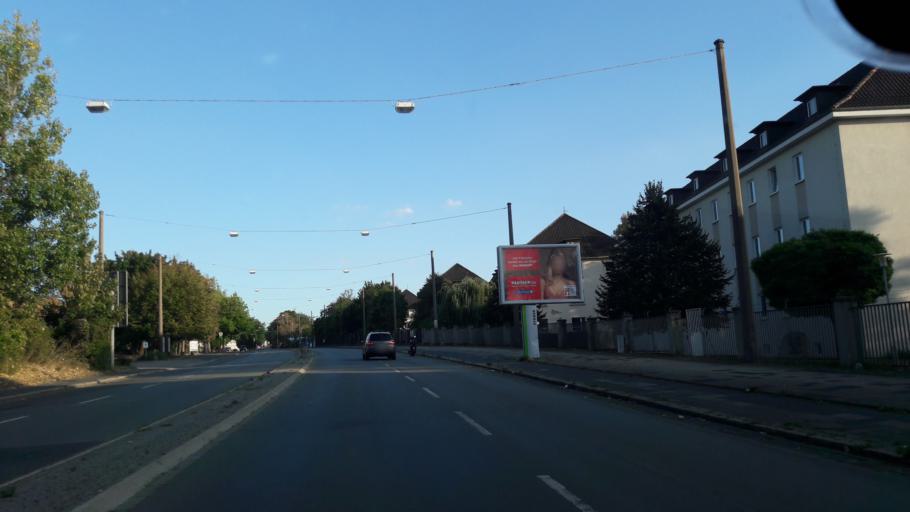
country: DE
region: Lower Saxony
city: Hildesheim
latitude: 52.1696
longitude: 9.9367
